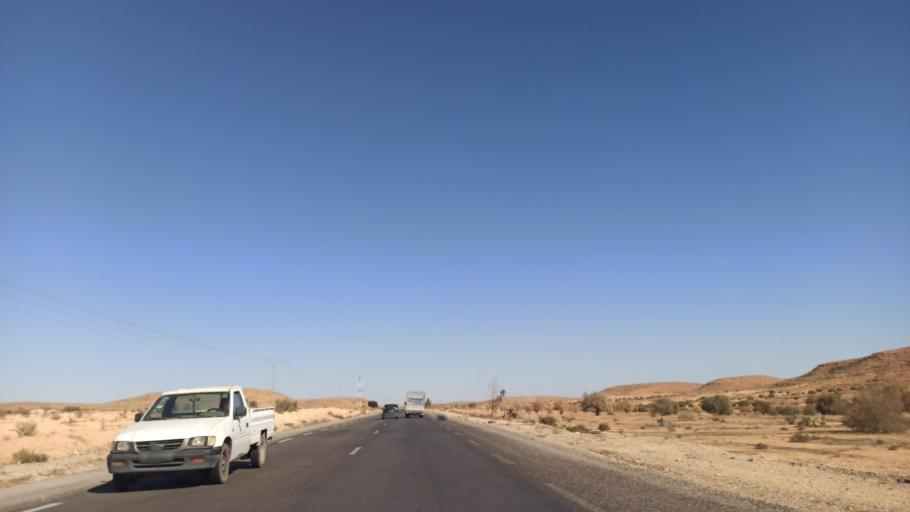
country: TN
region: Sidi Bu Zayd
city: Bi'r al Hufayy
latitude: 34.7101
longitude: 9.0493
